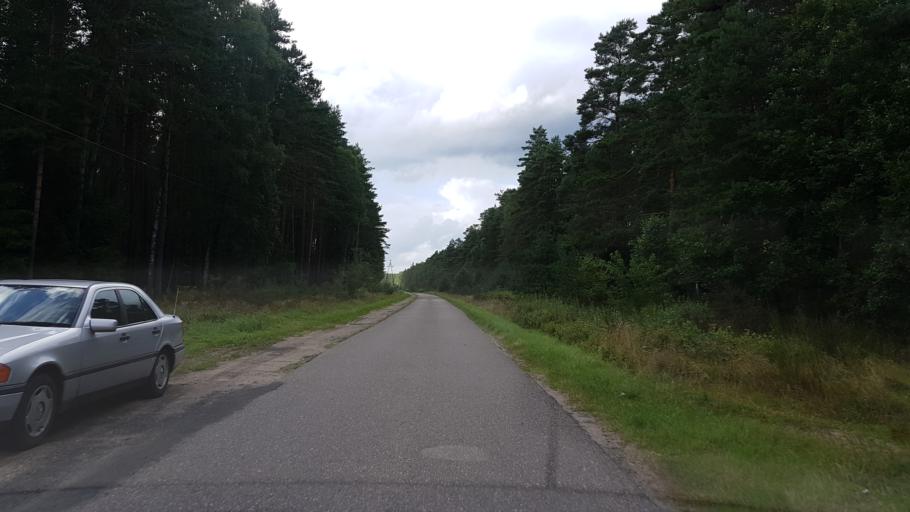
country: PL
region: West Pomeranian Voivodeship
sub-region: Powiat bialogardzki
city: Tychowo
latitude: 54.0339
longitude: 16.3424
